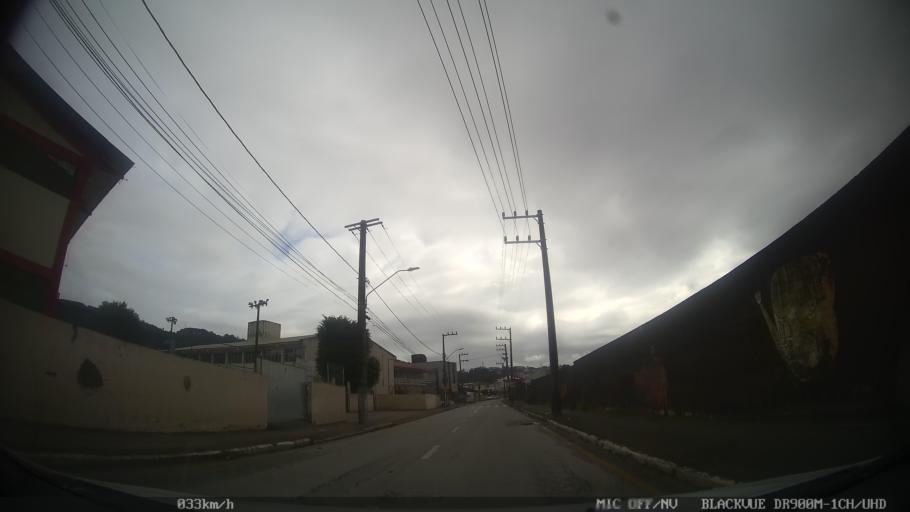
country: BR
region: Santa Catarina
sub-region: Sao Jose
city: Campinas
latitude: -27.5972
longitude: -48.6233
